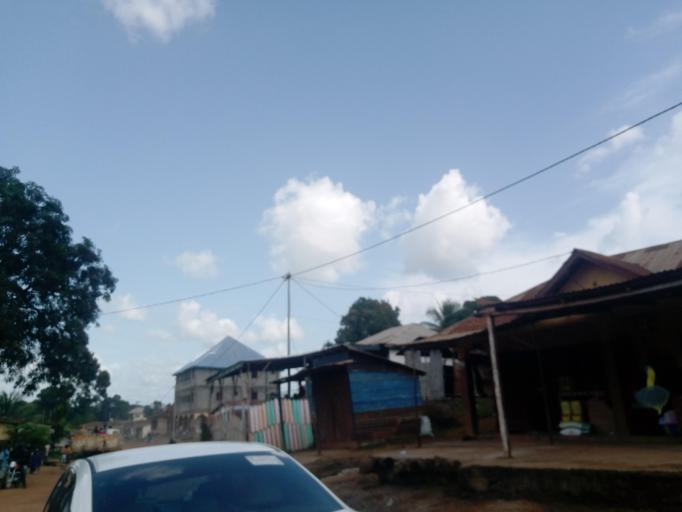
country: SL
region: Northern Province
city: Makeni
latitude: 8.8937
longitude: -12.0350
